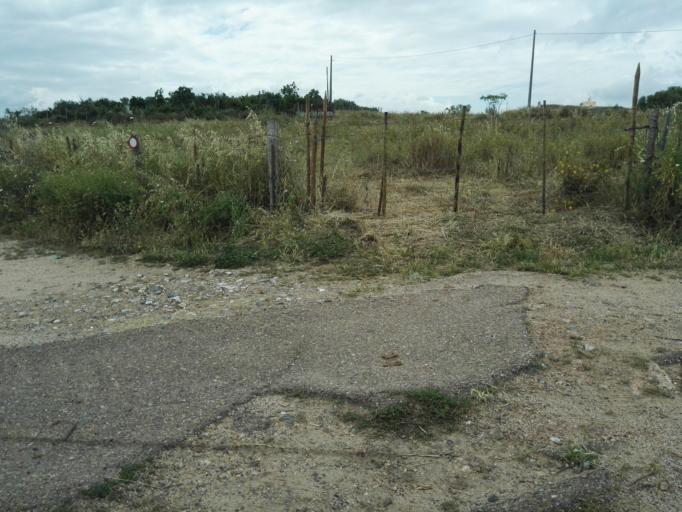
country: PT
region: Portalegre
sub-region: Elvas
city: Elvas
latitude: 38.8716
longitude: -7.1524
